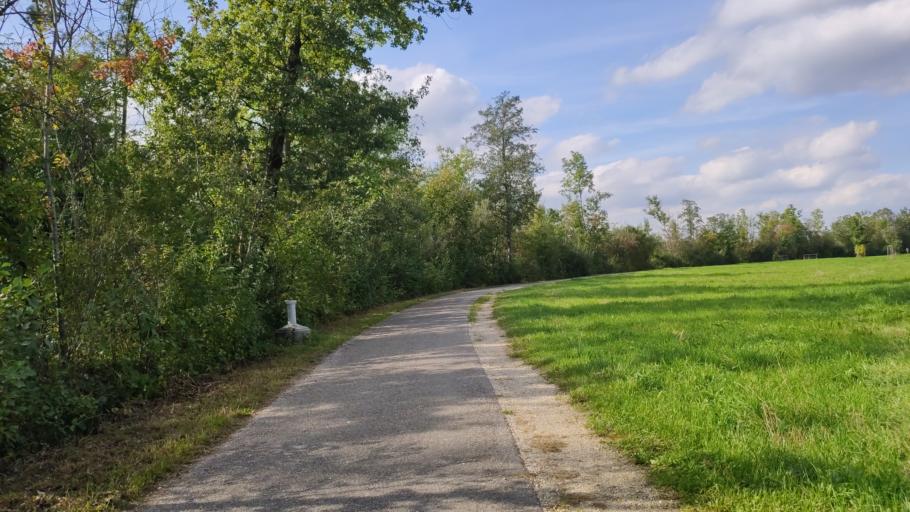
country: DE
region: Bavaria
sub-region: Upper Bavaria
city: Kaufering
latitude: 48.0973
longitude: 10.8672
